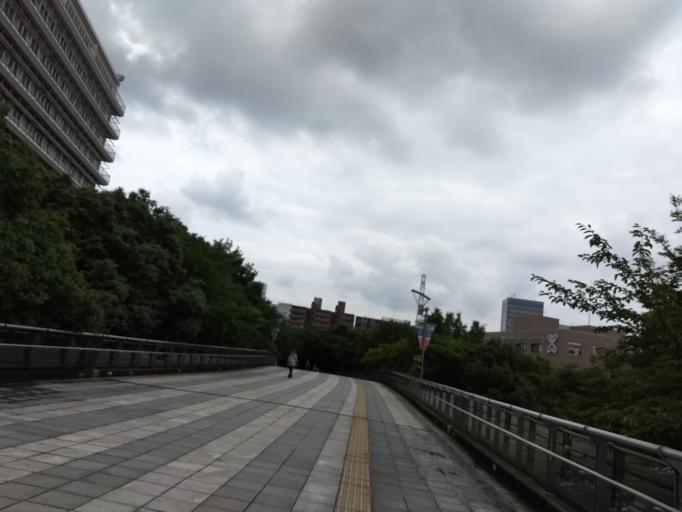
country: JP
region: Kanagawa
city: Yokohama
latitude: 35.5105
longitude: 139.6093
